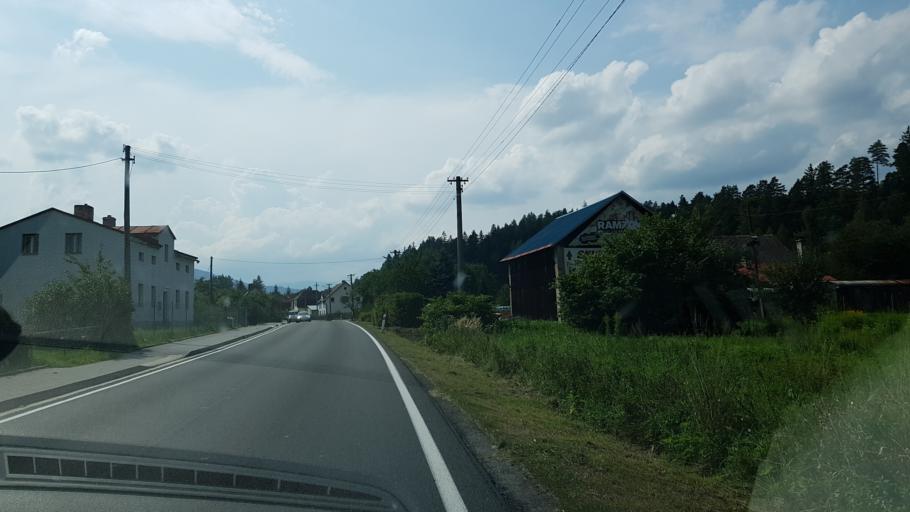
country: CZ
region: Olomoucky
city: Mikulovice
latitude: 50.2913
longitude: 17.2969
